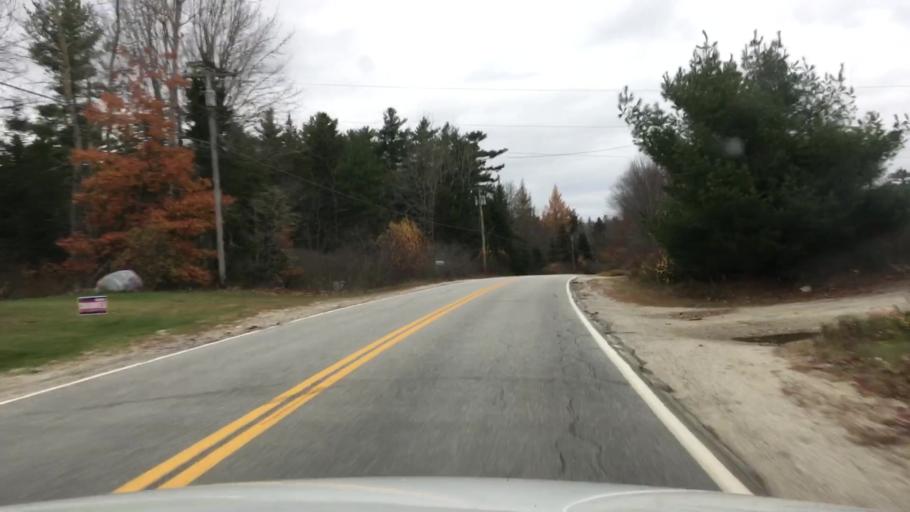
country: US
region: Maine
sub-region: Hancock County
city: Sedgwick
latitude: 44.2883
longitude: -68.5553
